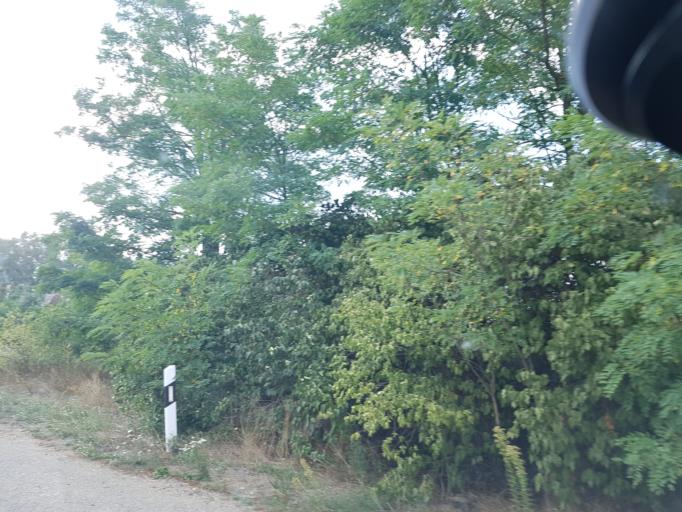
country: DE
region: Brandenburg
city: Bronkow
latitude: 51.7064
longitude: 13.8911
